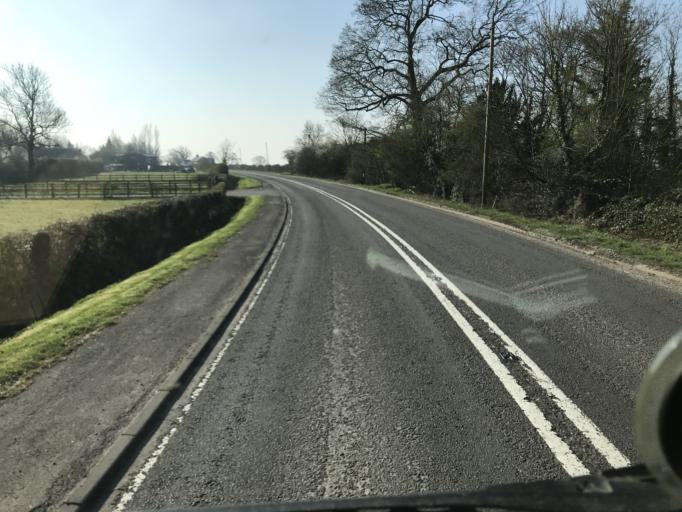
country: GB
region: England
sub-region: Cheshire West and Chester
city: Waverton
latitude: 53.1439
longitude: -2.8122
